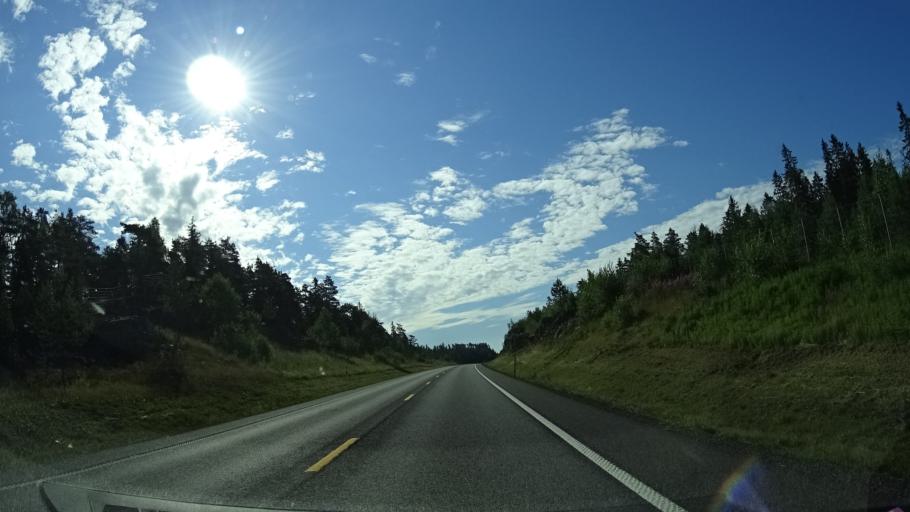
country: NO
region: Ostfold
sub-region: Marker
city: Orje
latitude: 59.5220
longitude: 11.5851
